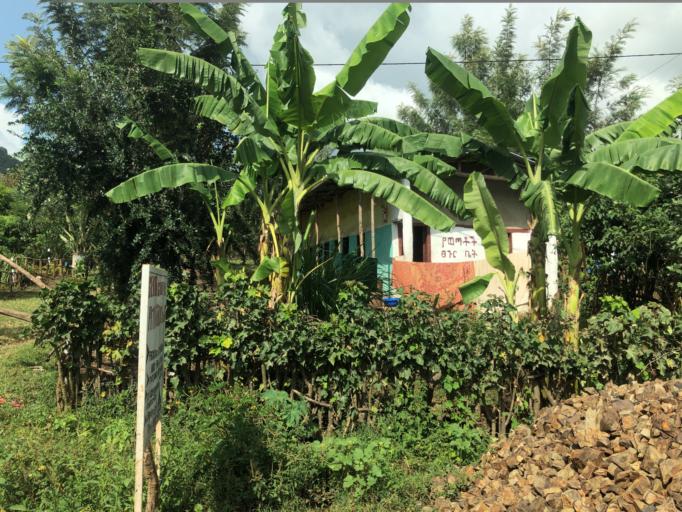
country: ET
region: Southern Nations, Nationalities, and People's Region
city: Bako
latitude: 5.7435
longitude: 36.5995
